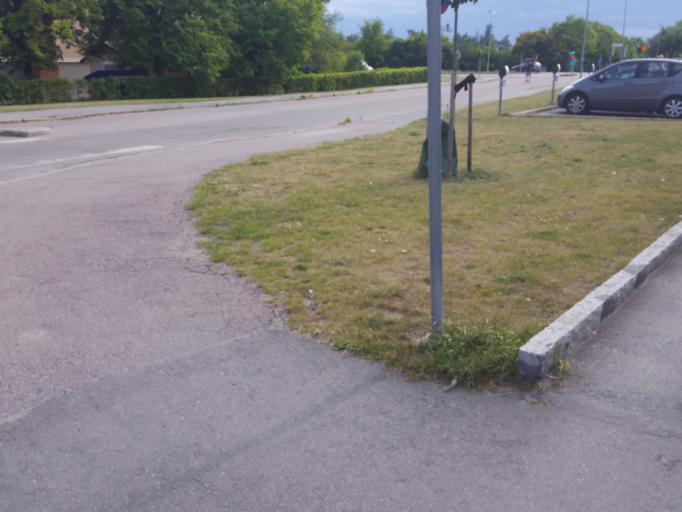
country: SE
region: Uppsala
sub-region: Uppsala Kommun
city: Uppsala
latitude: 59.8645
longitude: 17.6693
